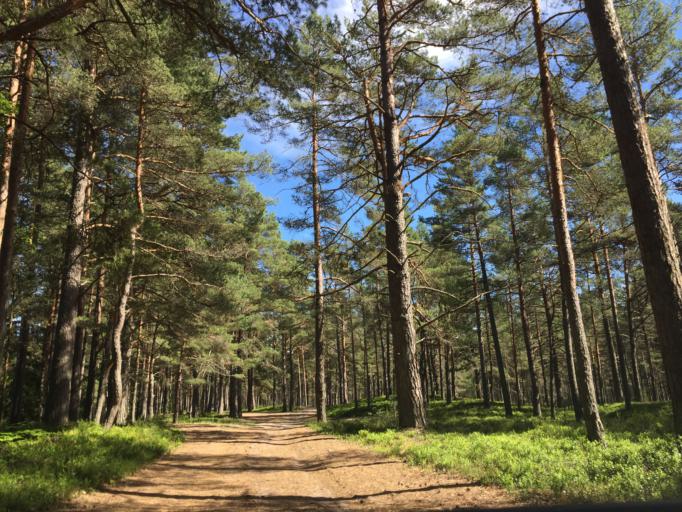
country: LV
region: Rojas
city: Roja
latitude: 57.5084
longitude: 22.7838
